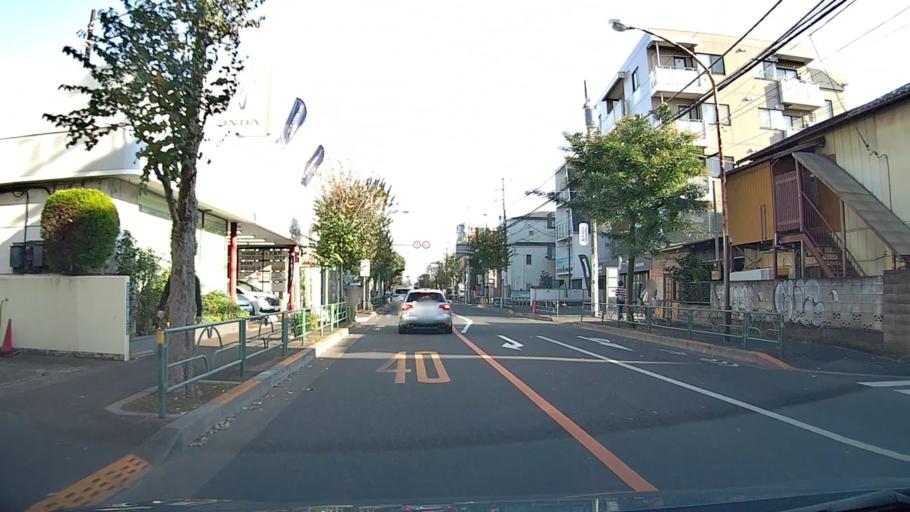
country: JP
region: Tokyo
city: Musashino
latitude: 35.7056
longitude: 139.5683
